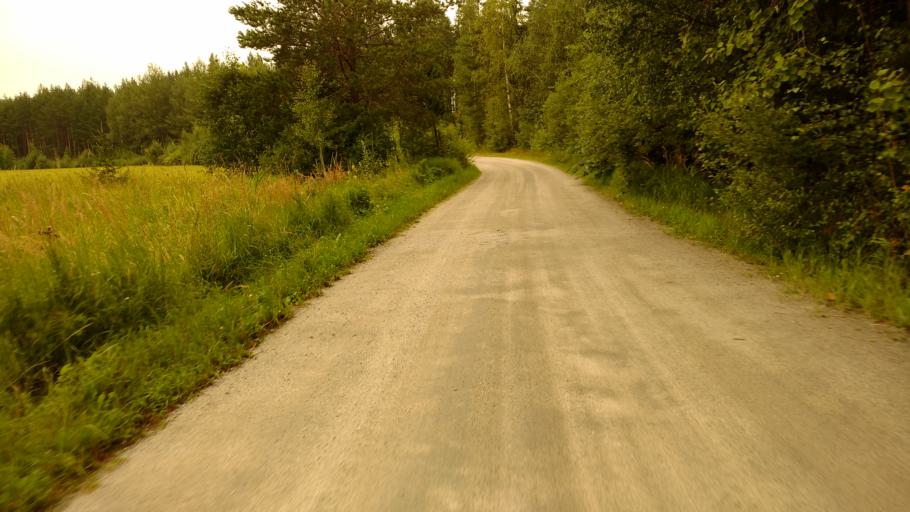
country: FI
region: Varsinais-Suomi
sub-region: Salo
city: Pertteli
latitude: 60.4094
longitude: 23.2252
